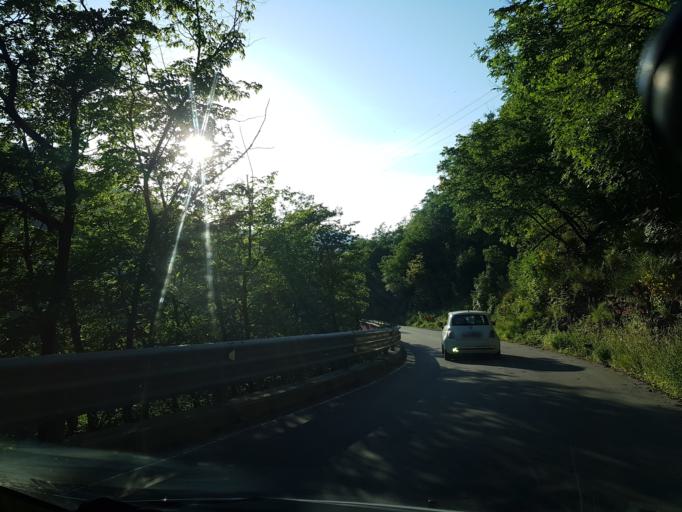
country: IT
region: Tuscany
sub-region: Provincia di Lucca
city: Minucciano
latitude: 44.1734
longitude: 10.2023
